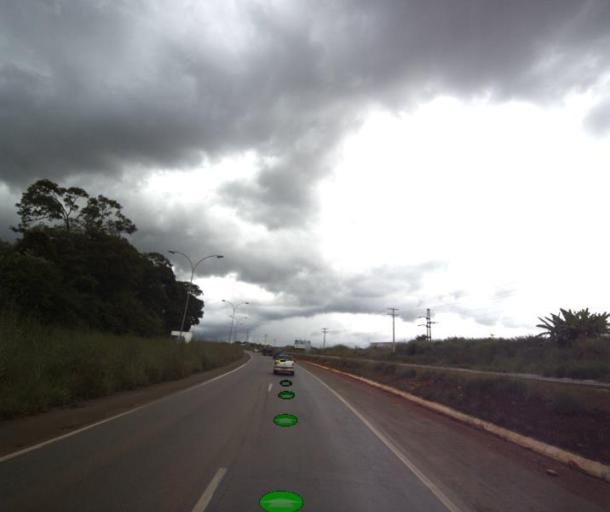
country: BR
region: Goias
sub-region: Anapolis
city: Anapolis
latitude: -16.2894
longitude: -48.9369
